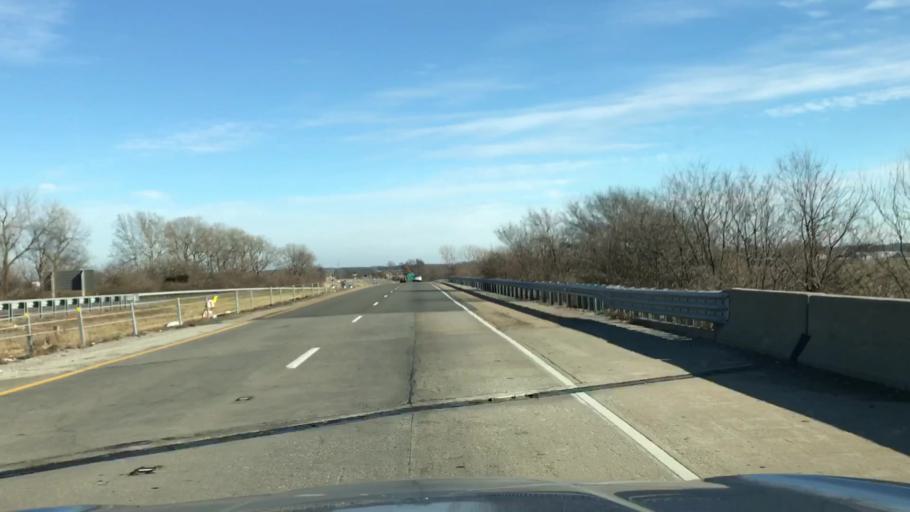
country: US
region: Illinois
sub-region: Madison County
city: Maryville
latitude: 38.7520
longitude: -89.9286
